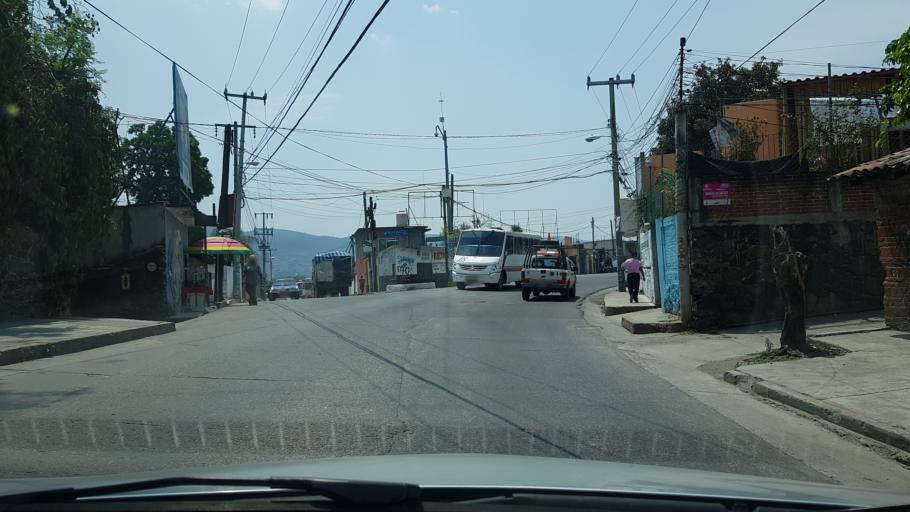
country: MX
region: Morelos
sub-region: Jiutepec
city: Jiutepec
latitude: 18.8769
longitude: -99.1728
